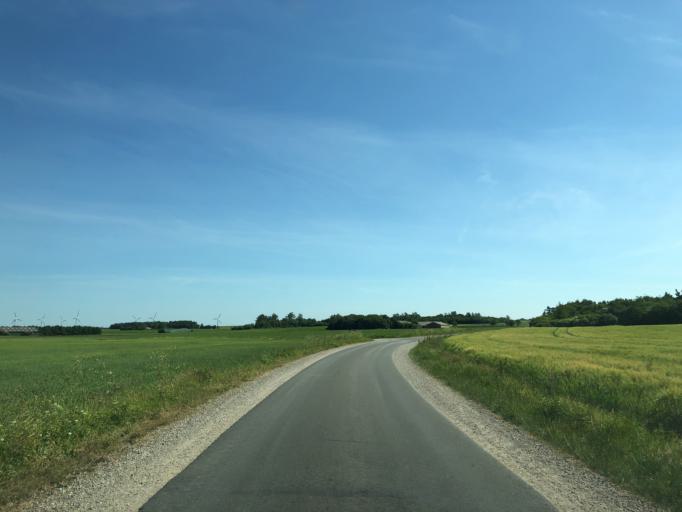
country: DK
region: Central Jutland
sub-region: Struer Kommune
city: Struer
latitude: 56.4301
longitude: 8.4652
